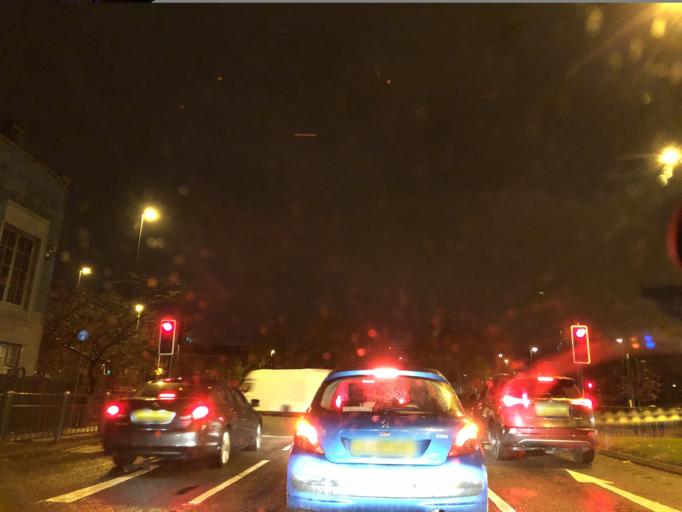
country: GB
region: England
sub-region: Borough of Oldham
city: Oldham
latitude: 53.5372
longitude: -2.1159
